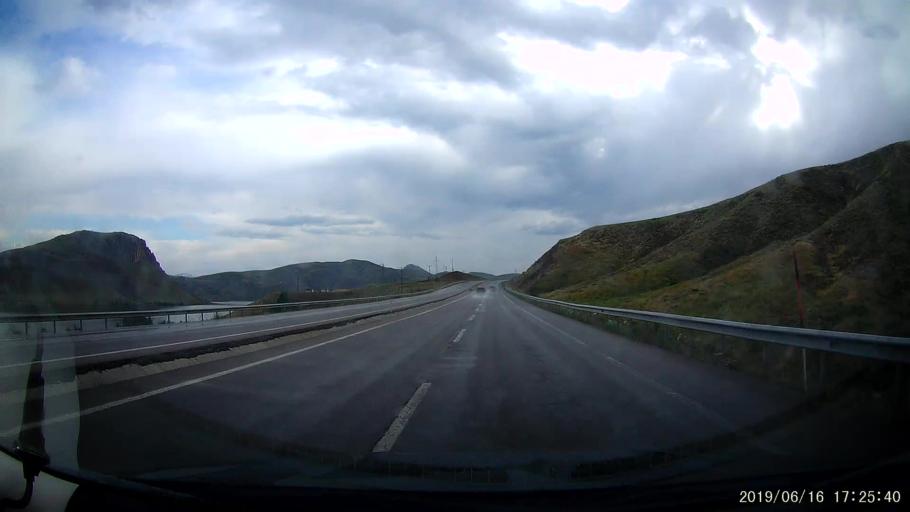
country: TR
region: Erzincan
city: Tercan
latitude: 39.7684
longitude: 40.4302
